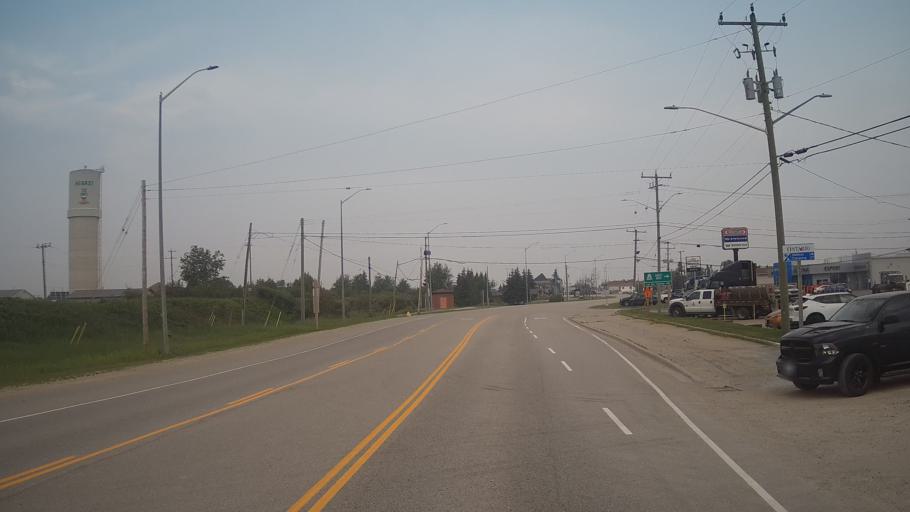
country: CA
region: Ontario
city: Hearst
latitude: 49.6883
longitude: -83.6475
